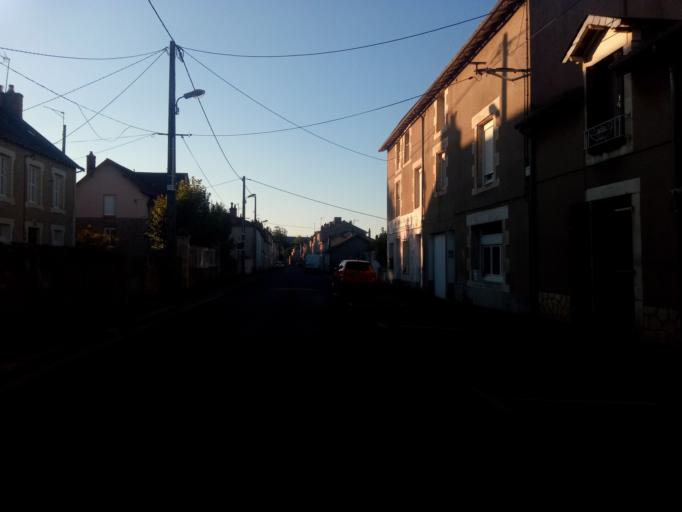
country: FR
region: Poitou-Charentes
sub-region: Departement de la Vienne
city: Montmorillon
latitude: 46.4205
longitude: 0.8704
